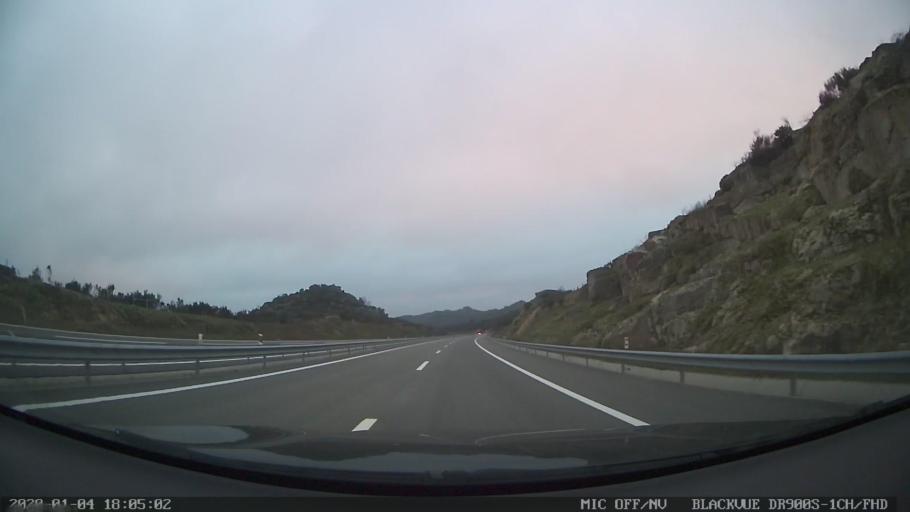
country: PT
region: Vila Real
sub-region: Vila Pouca de Aguiar
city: Vila Pouca de Aguiar
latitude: 41.4061
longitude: -7.6429
